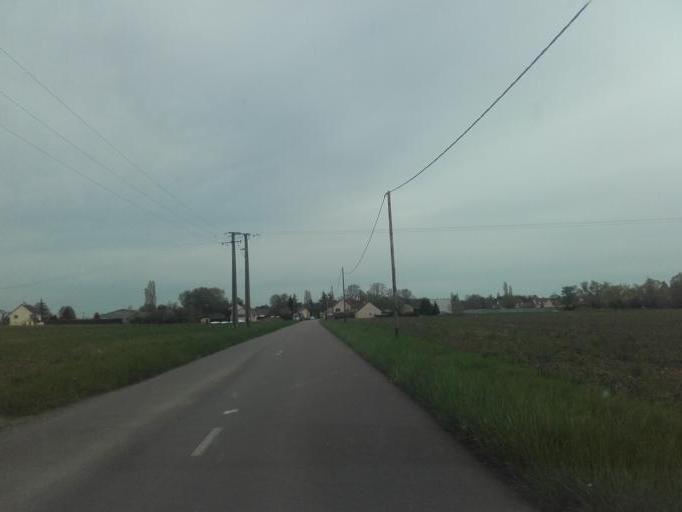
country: FR
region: Bourgogne
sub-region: Departement de Saone-et-Loire
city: Demigny
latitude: 46.9538
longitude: 4.8359
